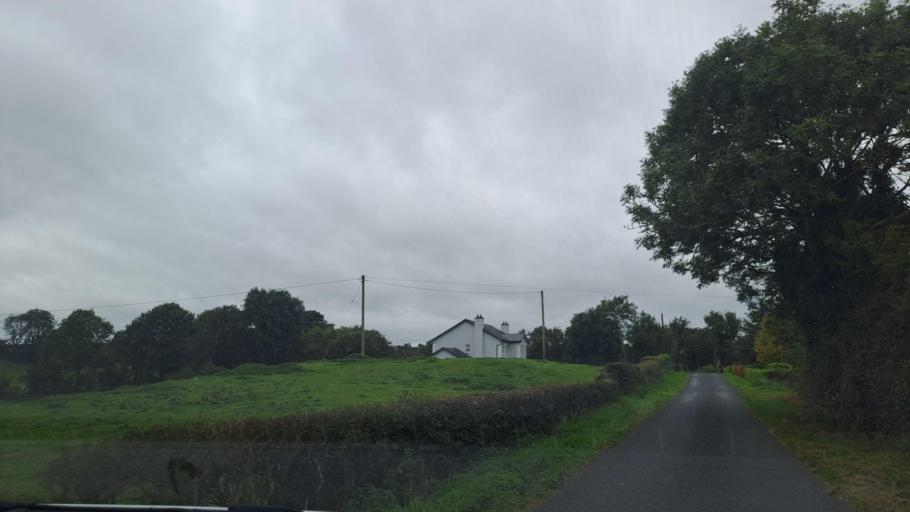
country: IE
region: Ulster
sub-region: An Cabhan
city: Kingscourt
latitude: 54.0059
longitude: -6.8635
